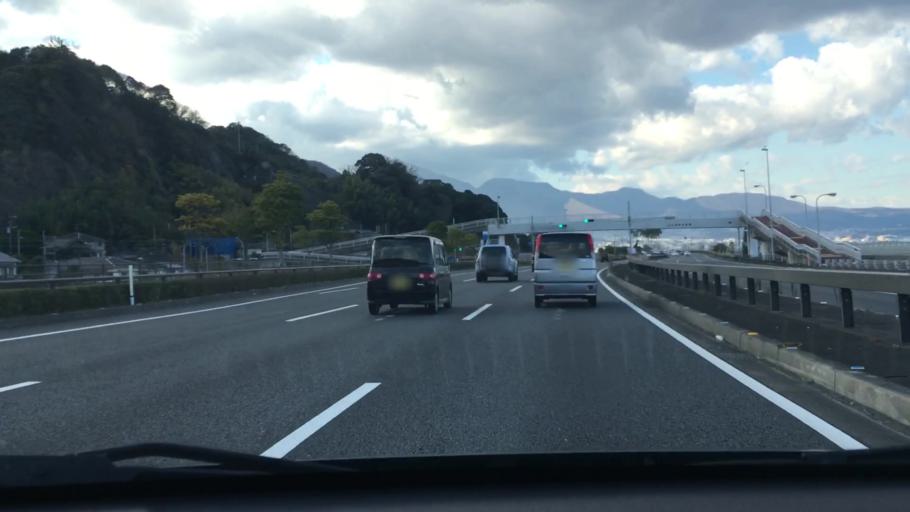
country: JP
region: Oita
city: Oita
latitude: 33.2530
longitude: 131.5652
